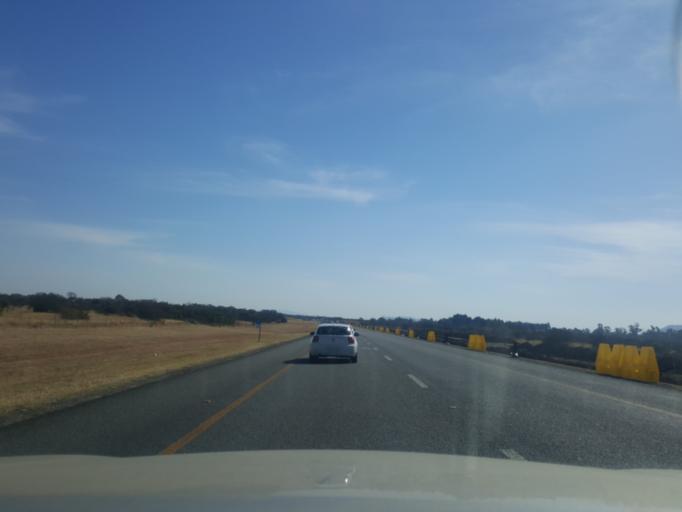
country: ZA
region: North-West
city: Ga-Rankuwa
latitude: -25.6517
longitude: 27.9723
